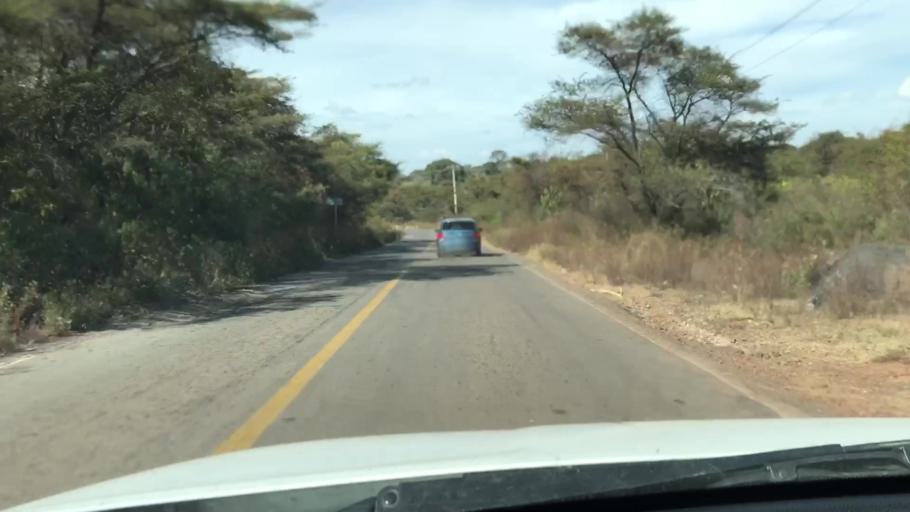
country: MX
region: Jalisco
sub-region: Zacoalco de Torres
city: Barranca de Otates (Barranca de Otatan)
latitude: 20.1973
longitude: -103.6938
